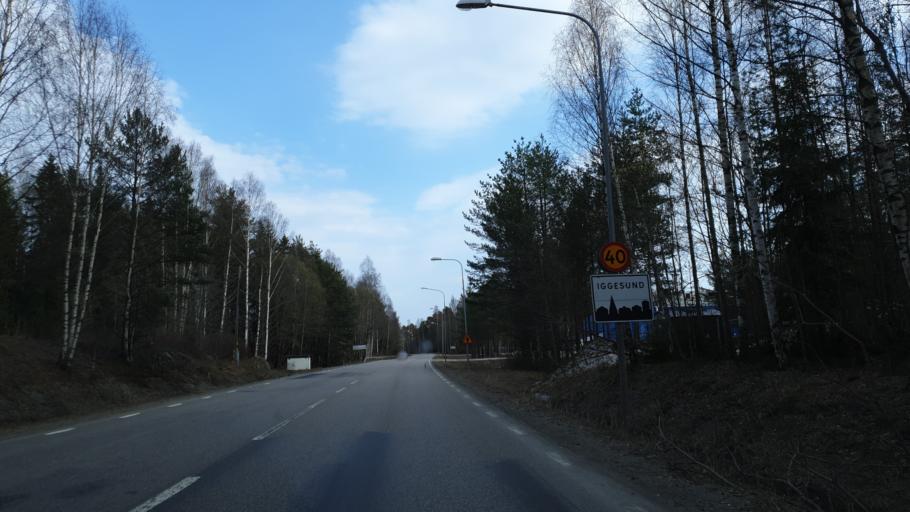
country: SE
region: Gaevleborg
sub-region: Hudiksvalls Kommun
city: Iggesund
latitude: 61.6431
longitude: 17.0618
